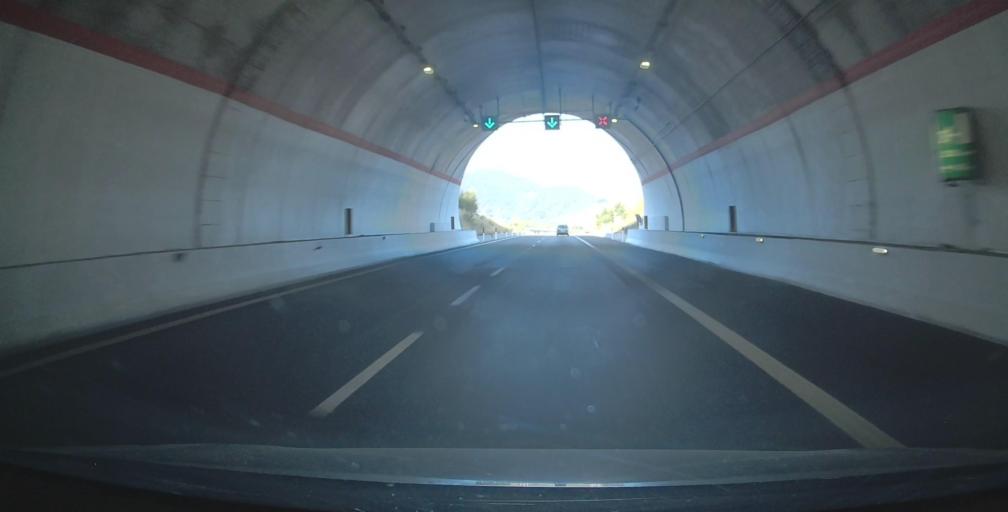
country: IT
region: Calabria
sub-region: Provincia di Cosenza
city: Morano Calabro
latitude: 39.8656
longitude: 16.0934
